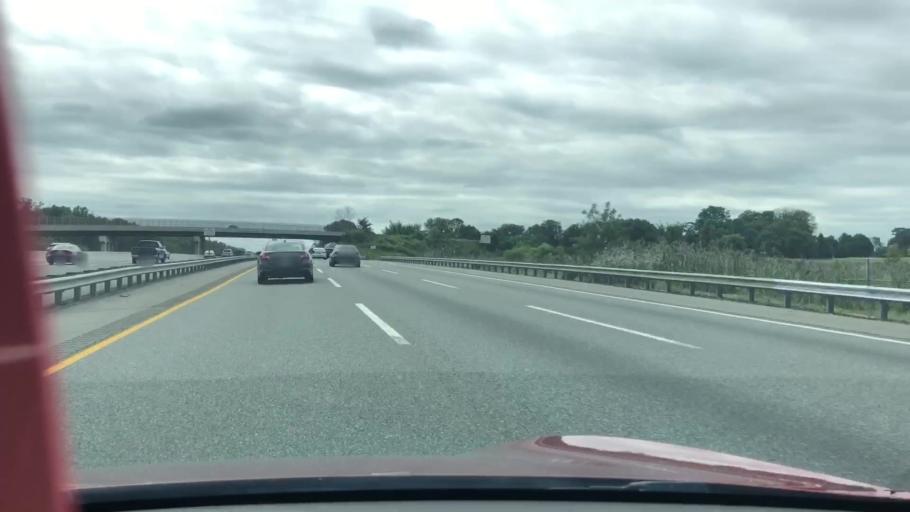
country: US
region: New Jersey
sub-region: Mercer County
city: Groveville
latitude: 40.1562
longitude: -74.6610
